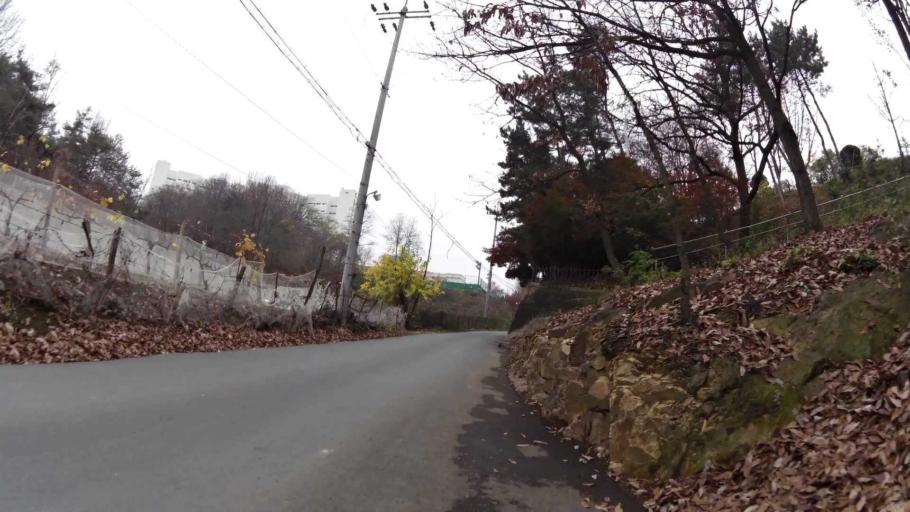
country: KR
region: Daegu
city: Daegu
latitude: 35.8578
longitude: 128.6603
